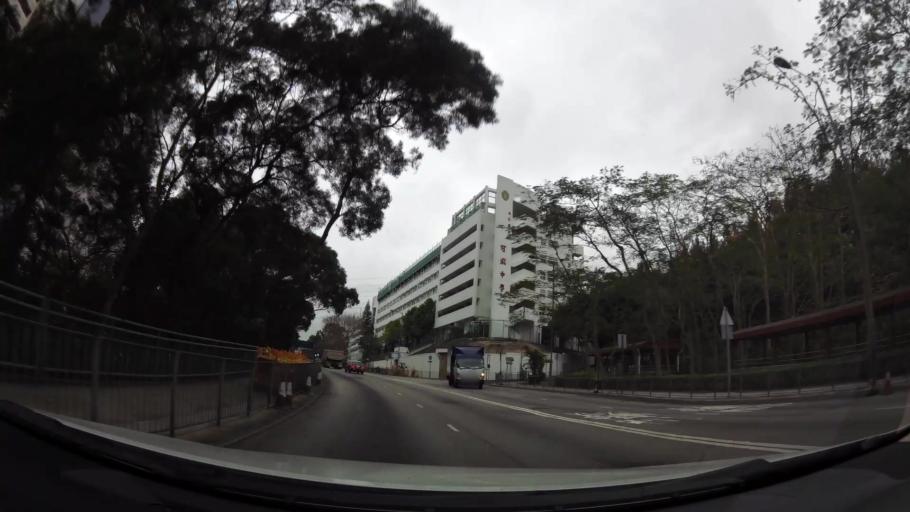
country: HK
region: Tsuen Wan
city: Tsuen Wan
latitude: 22.3803
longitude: 114.1365
